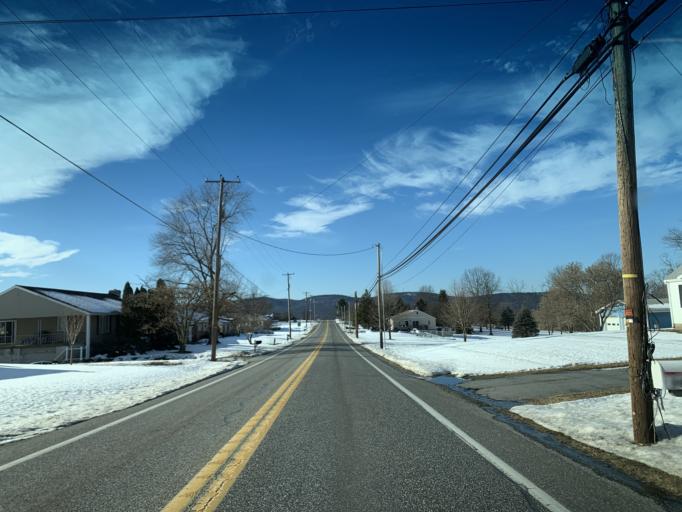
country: US
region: Pennsylvania
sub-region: York County
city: Dillsburg
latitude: 40.0902
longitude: -77.0259
